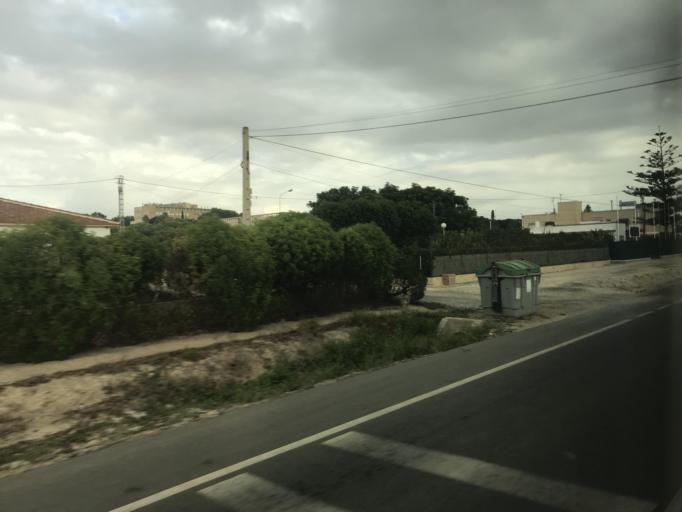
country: ES
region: Valencia
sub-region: Provincia de Alicante
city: Guardamar del Segura
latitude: 38.1244
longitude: -0.6523
